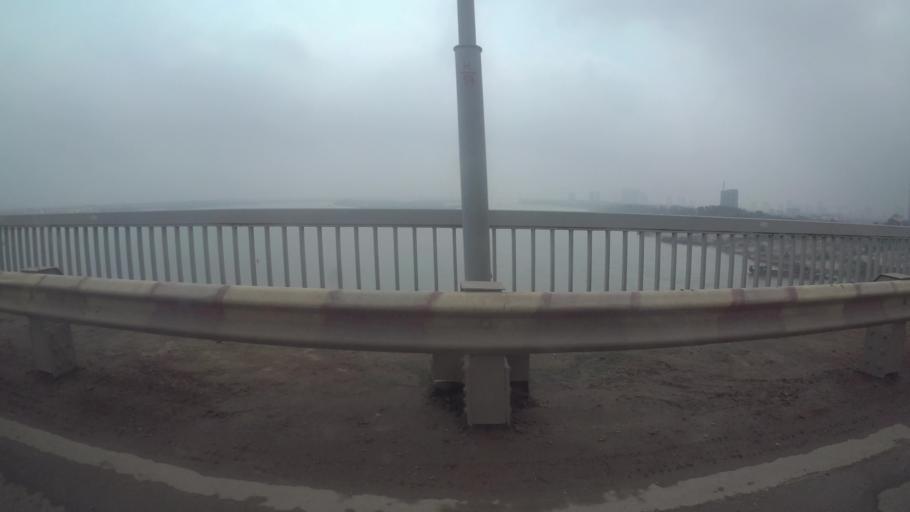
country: VN
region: Ha Noi
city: Tay Ho
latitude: 21.0963
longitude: 105.7864
